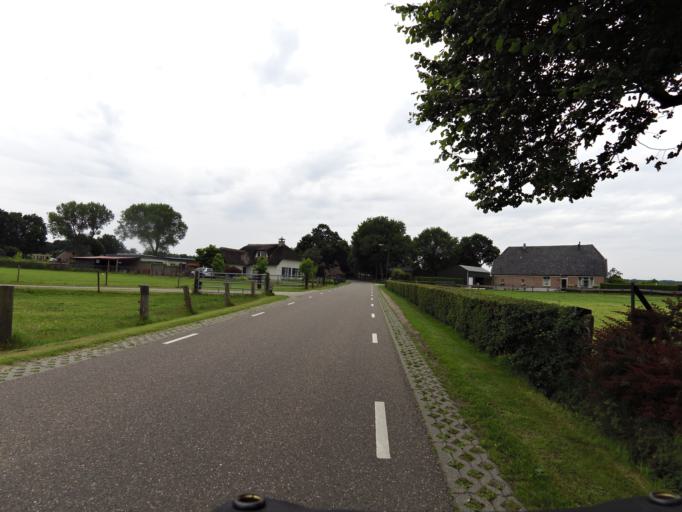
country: NL
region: Gelderland
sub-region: Gemeente Apeldoorn
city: Beekbergen
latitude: 52.1549
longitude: 6.0031
